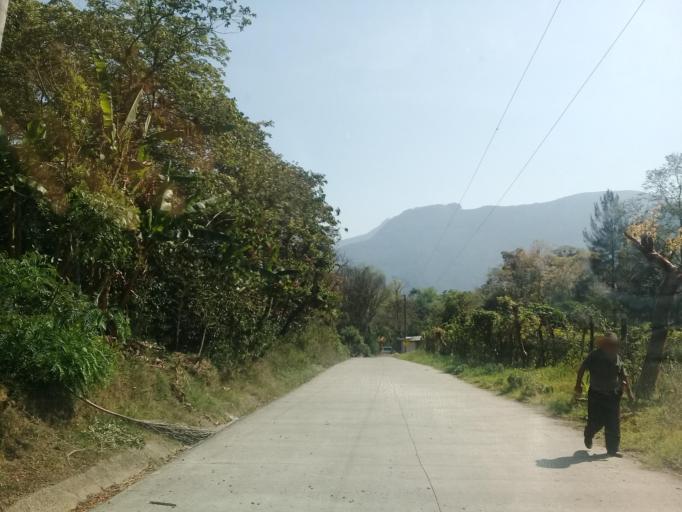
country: MX
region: Veracruz
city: Rafael Delgado
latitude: 18.7803
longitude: -97.0213
